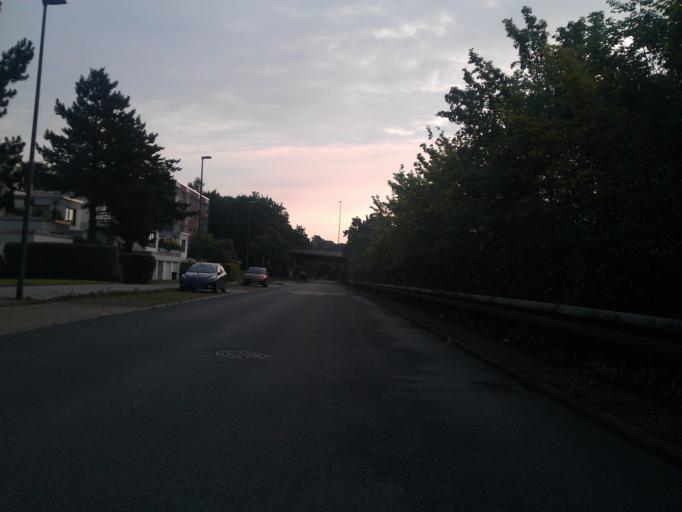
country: DE
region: North Rhine-Westphalia
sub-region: Regierungsbezirk Koln
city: Aachen
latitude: 50.7712
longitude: 6.0561
